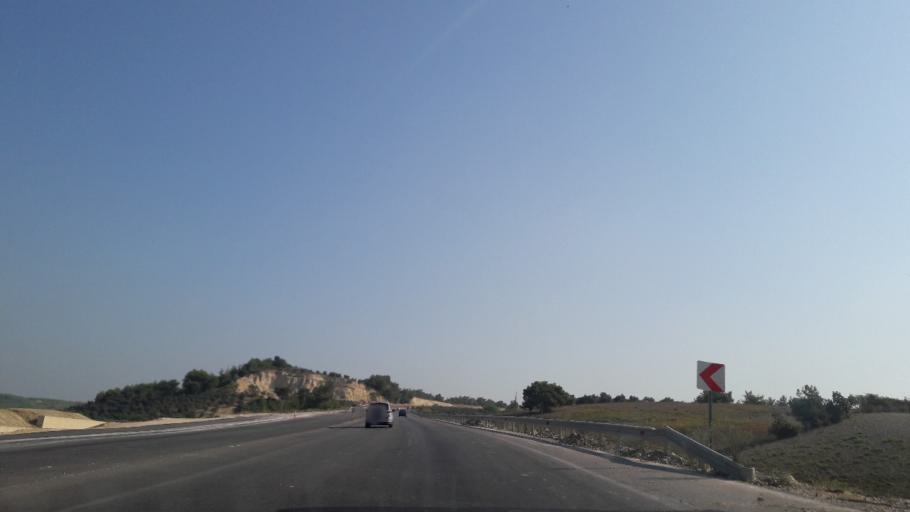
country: TR
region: Adana
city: Yuregir
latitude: 37.0764
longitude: 35.4708
